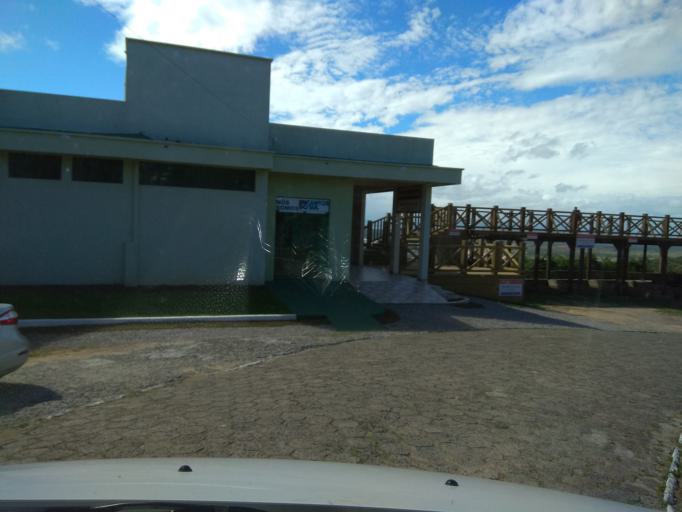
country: BR
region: Santa Catarina
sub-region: Laguna
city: Laguna
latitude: -28.4883
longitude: -48.7791
